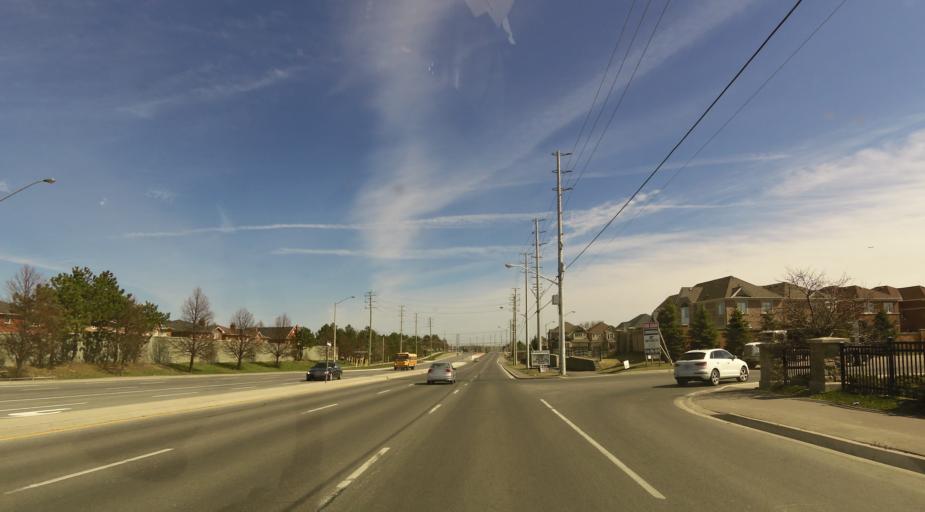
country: CA
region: Ontario
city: Brampton
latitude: 43.6460
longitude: -79.7535
